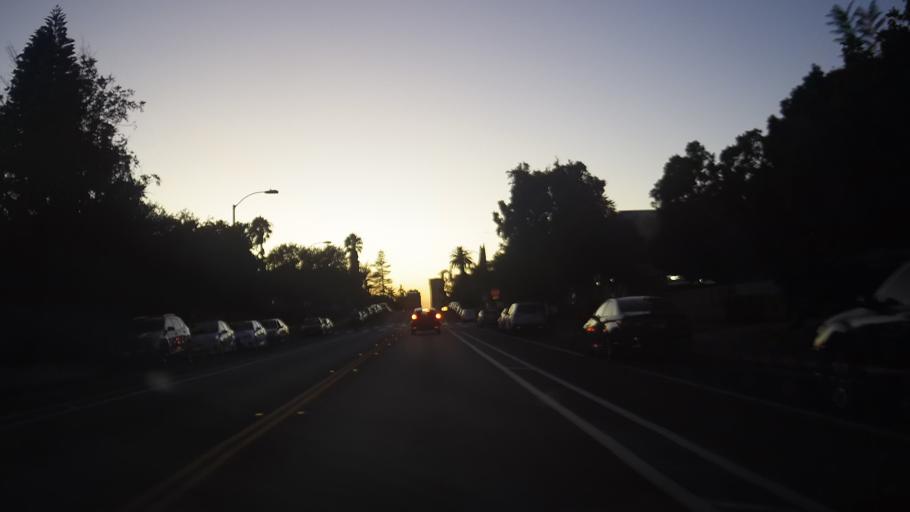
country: US
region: California
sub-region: San Diego County
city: San Diego
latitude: 32.7179
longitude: -117.1373
